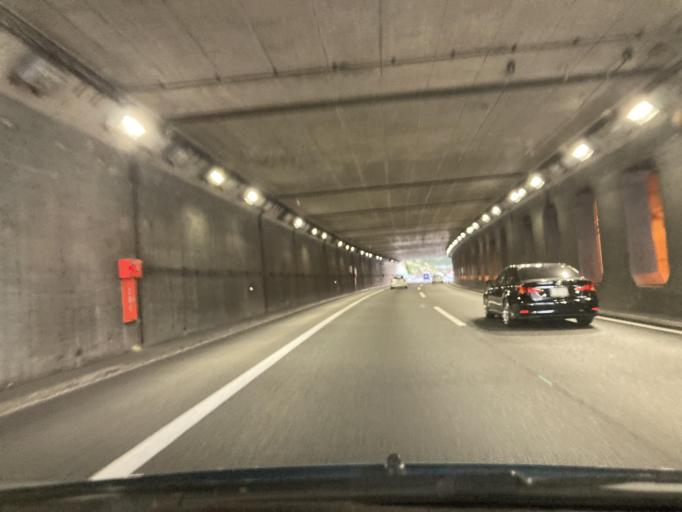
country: JP
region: Okinawa
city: Okinawa
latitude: 26.3201
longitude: 127.7896
